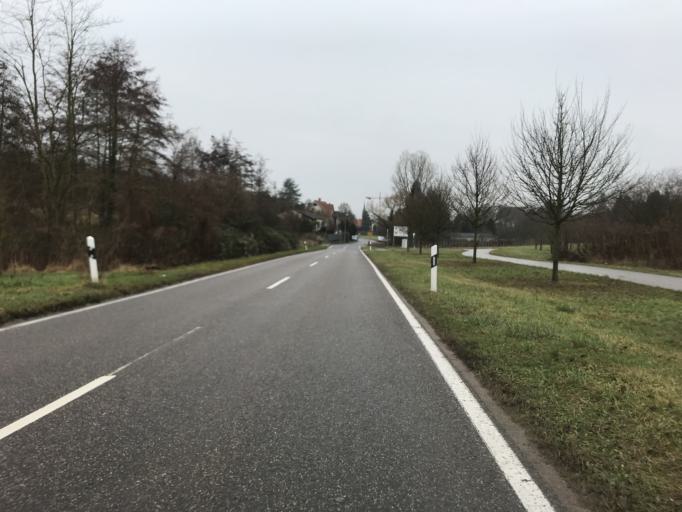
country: DE
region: Rheinland-Pfalz
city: Wackernheim
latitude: 49.9869
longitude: 8.1128
